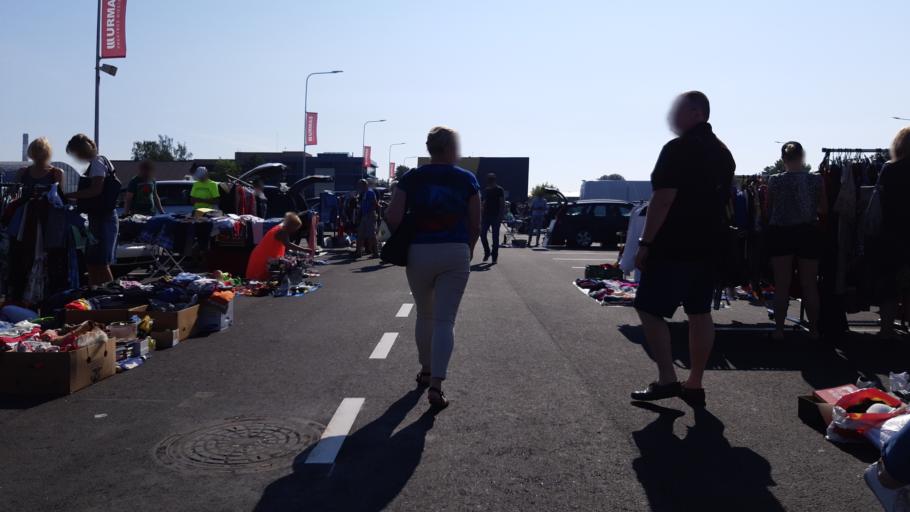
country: LT
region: Kauno apskritis
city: Dainava (Kaunas)
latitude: 54.9139
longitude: 23.9961
